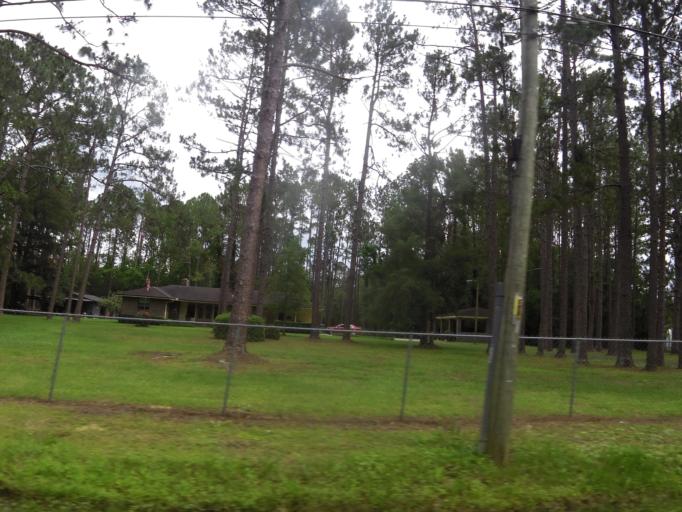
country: US
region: Florida
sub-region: Nassau County
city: Nassau Village-Ratliff
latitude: 30.5272
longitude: -81.7352
